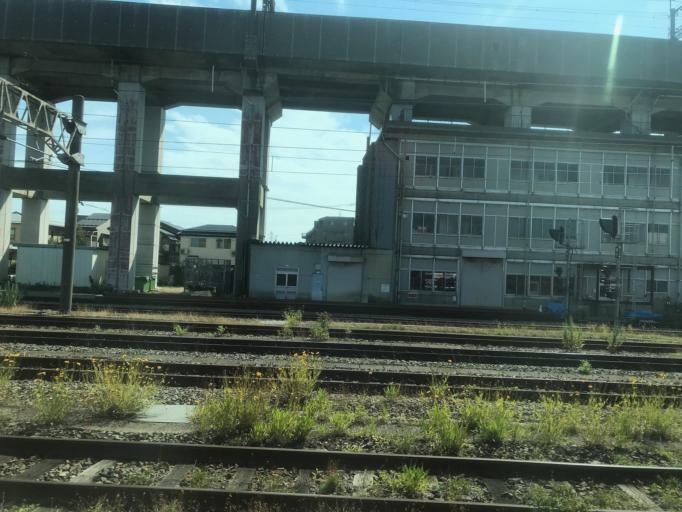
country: JP
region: Niigata
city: Kameda-honcho
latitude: 37.9087
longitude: 139.0814
